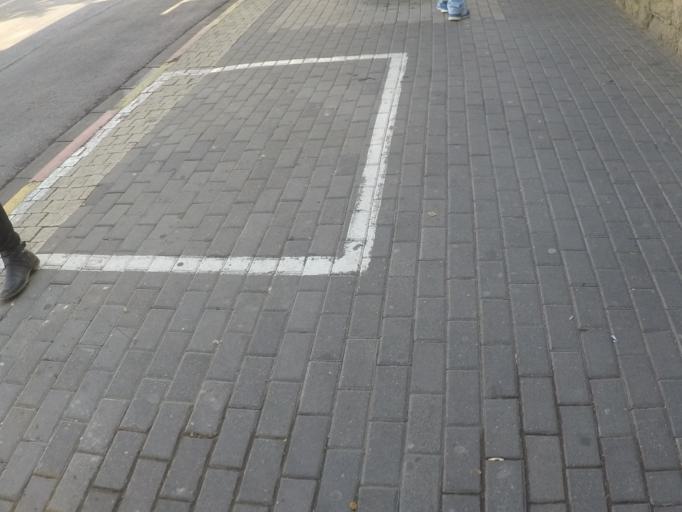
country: IL
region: Tel Aviv
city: Ramat Gan
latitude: 32.1078
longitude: 34.7984
